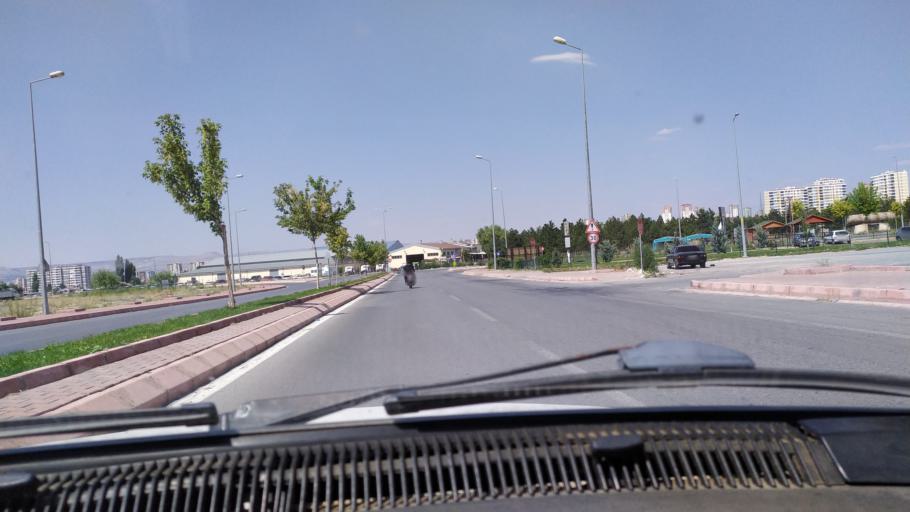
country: TR
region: Kayseri
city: Talas
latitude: 38.7183
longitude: 35.5555
